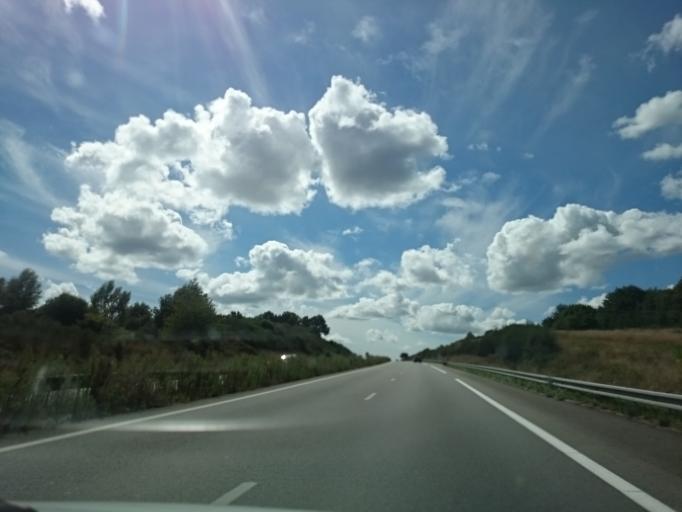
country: FR
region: Pays de la Loire
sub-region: Departement de la Loire-Atlantique
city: Couffe
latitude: 47.3689
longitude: -1.2978
